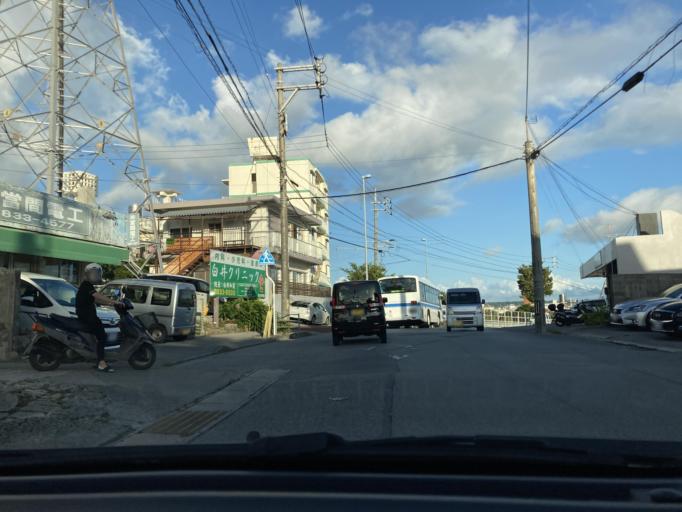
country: JP
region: Okinawa
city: Naha-shi
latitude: 26.2046
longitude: 127.7182
